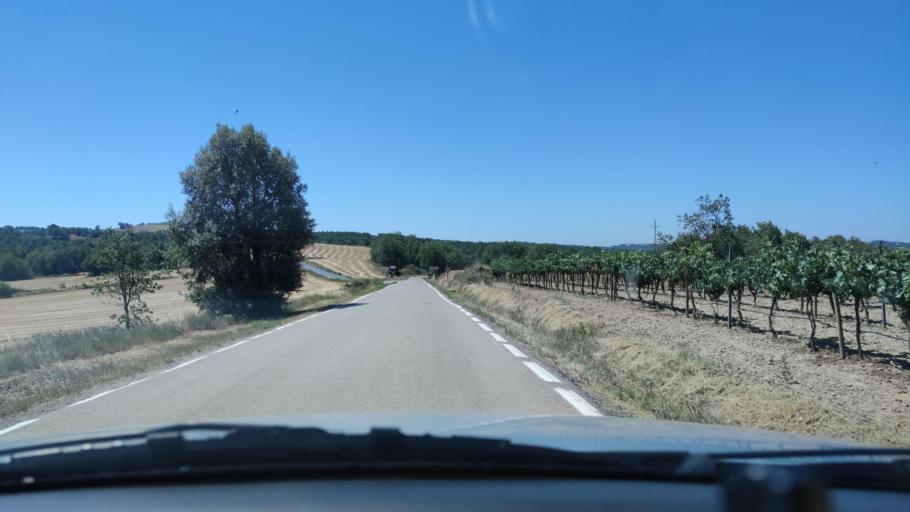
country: ES
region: Catalonia
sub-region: Provincia de Lleida
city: Solsona
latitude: 41.9189
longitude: 1.4608
